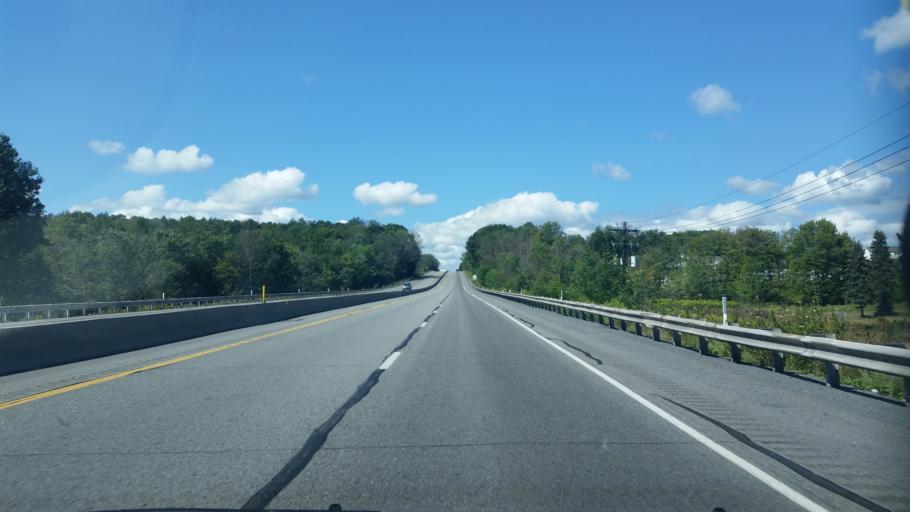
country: US
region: Pennsylvania
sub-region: Cambria County
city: Ebensburg
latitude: 40.4767
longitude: -78.7303
